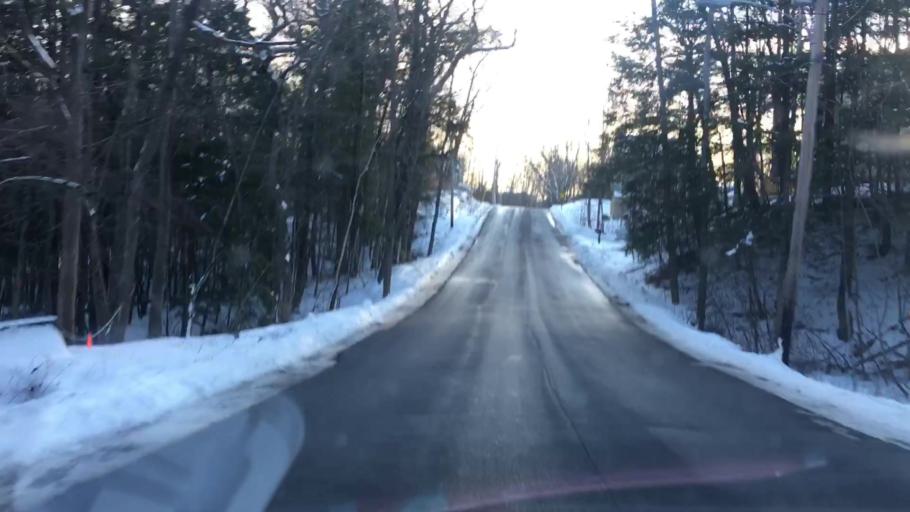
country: US
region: Maine
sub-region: Kennebec County
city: Gardiner
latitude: 44.2239
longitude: -69.7866
